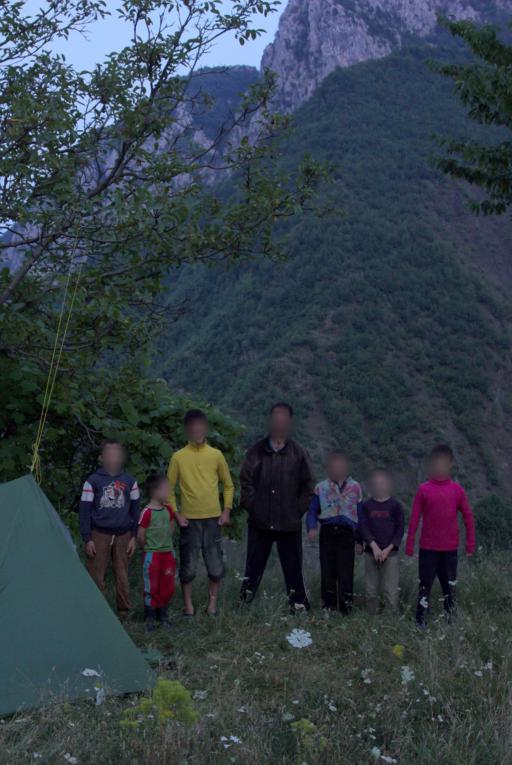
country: AL
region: Diber
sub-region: Rrethi i Dibres
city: Fushe-Lure
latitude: 41.7584
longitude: 20.2244
